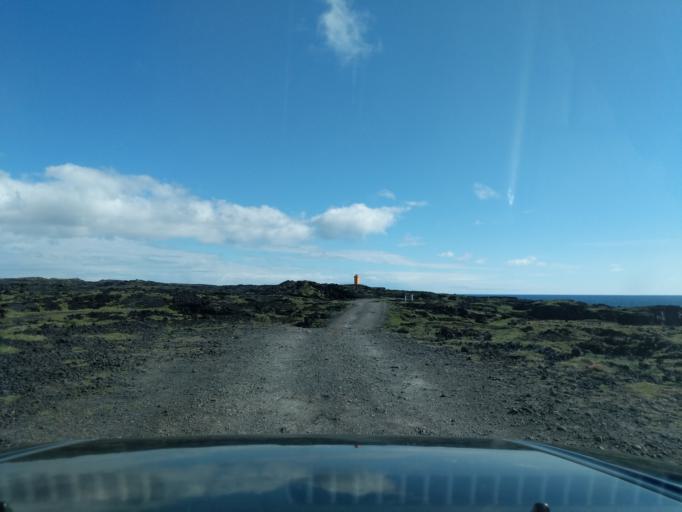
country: IS
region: West
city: Olafsvik
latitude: 64.8686
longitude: -24.0397
